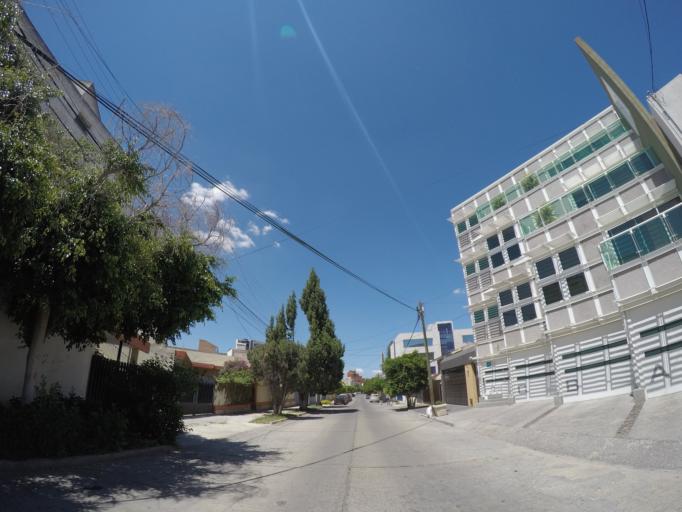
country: MX
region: San Luis Potosi
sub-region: San Luis Potosi
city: San Luis Potosi
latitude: 22.1446
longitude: -101.0095
